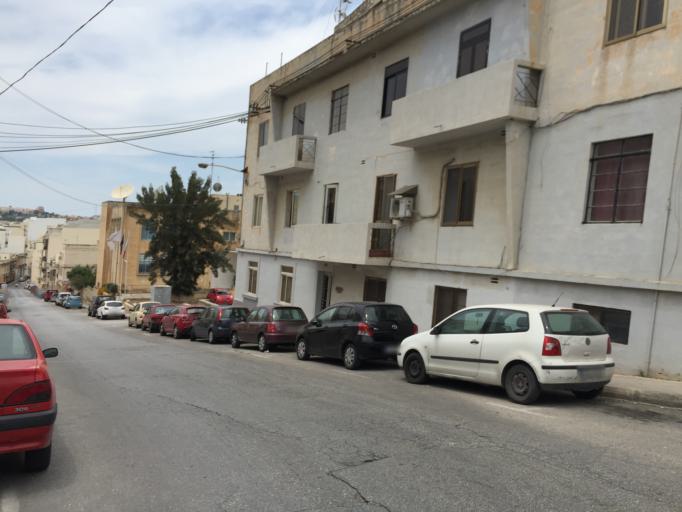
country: MT
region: Tal-Pieta
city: Pieta
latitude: 35.8923
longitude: 14.4930
